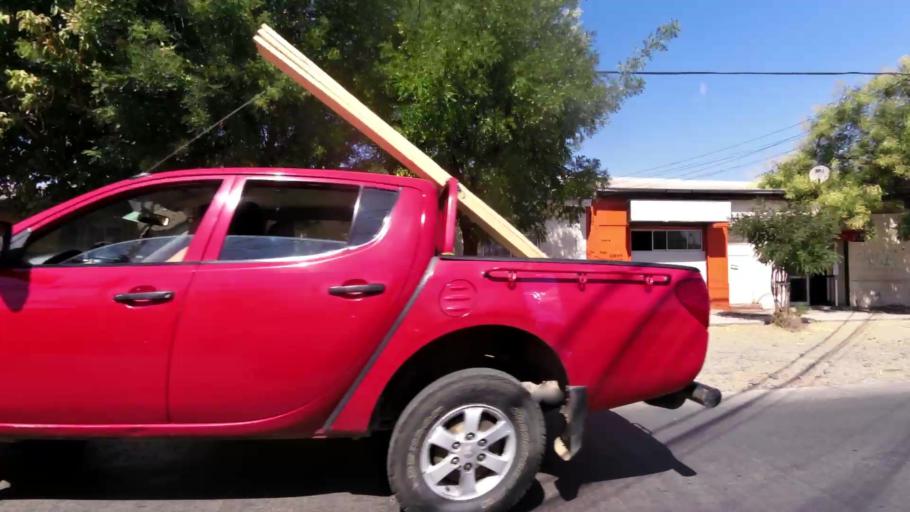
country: CL
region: Maule
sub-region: Provincia de Talca
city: Talca
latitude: -35.4385
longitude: -71.6514
